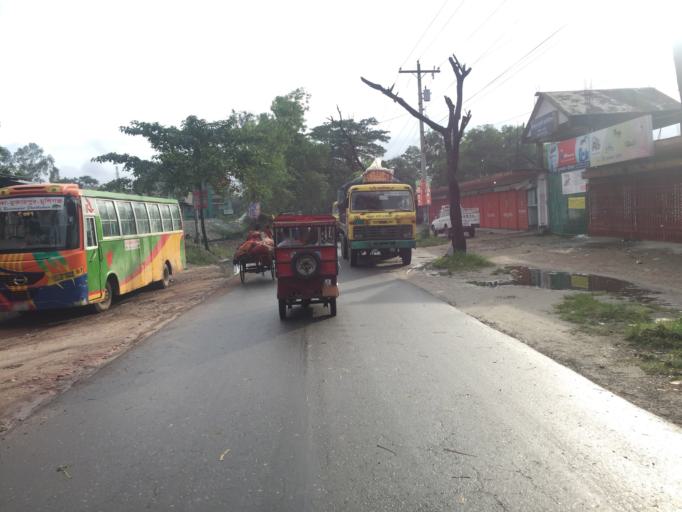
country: BD
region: Dhaka
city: Narayanganj
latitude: 23.5548
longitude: 90.5052
